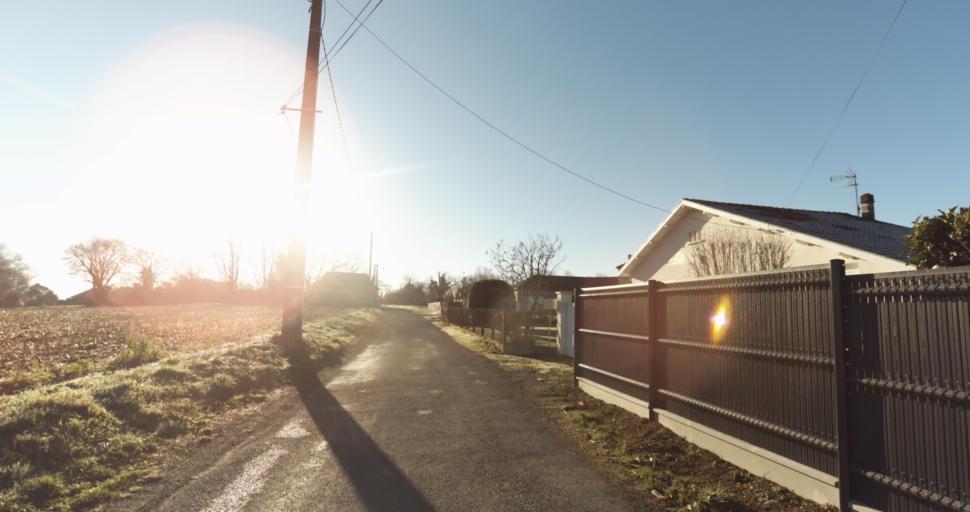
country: FR
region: Aquitaine
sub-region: Departement des Pyrenees-Atlantiques
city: Morlaas
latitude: 43.3338
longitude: -0.2640
